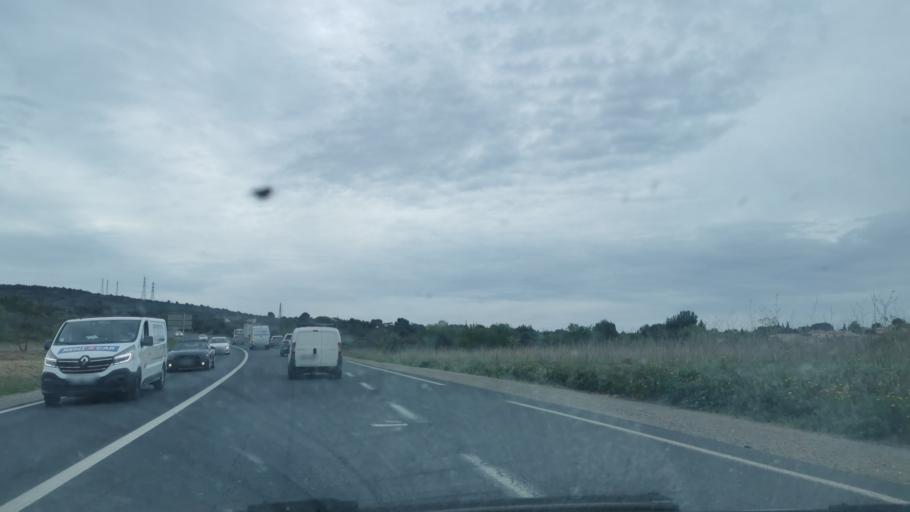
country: FR
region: Languedoc-Roussillon
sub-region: Departement de l'Herault
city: Balaruc-le-Vieux
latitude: 43.4596
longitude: 3.6953
